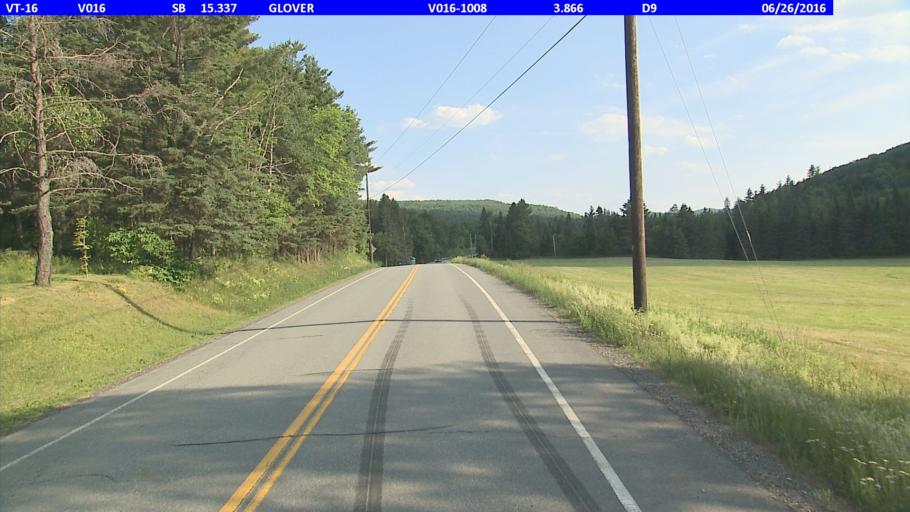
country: US
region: Vermont
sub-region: Caledonia County
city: Lyndonville
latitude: 44.6778
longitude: -72.1900
